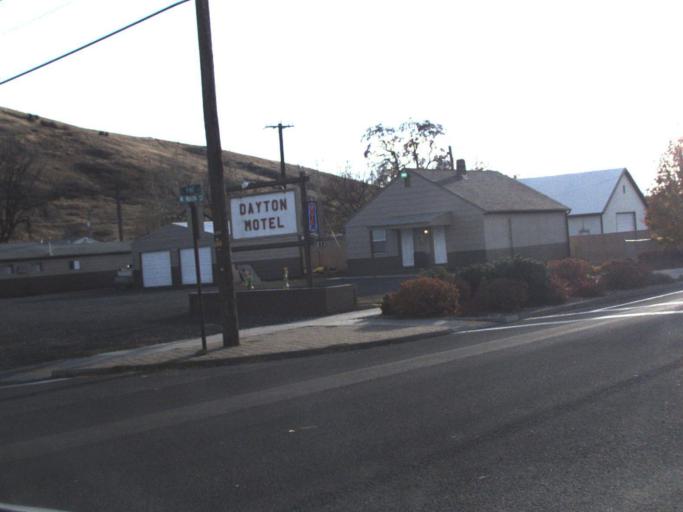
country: US
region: Washington
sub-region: Columbia County
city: Dayton
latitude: 46.3157
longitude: -117.9894
